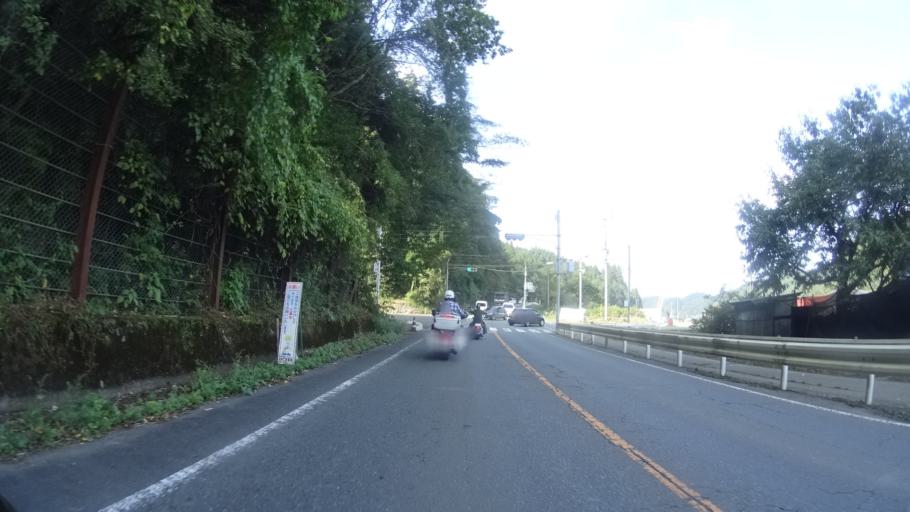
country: JP
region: Kumamoto
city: Aso
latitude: 33.0925
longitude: 131.0665
